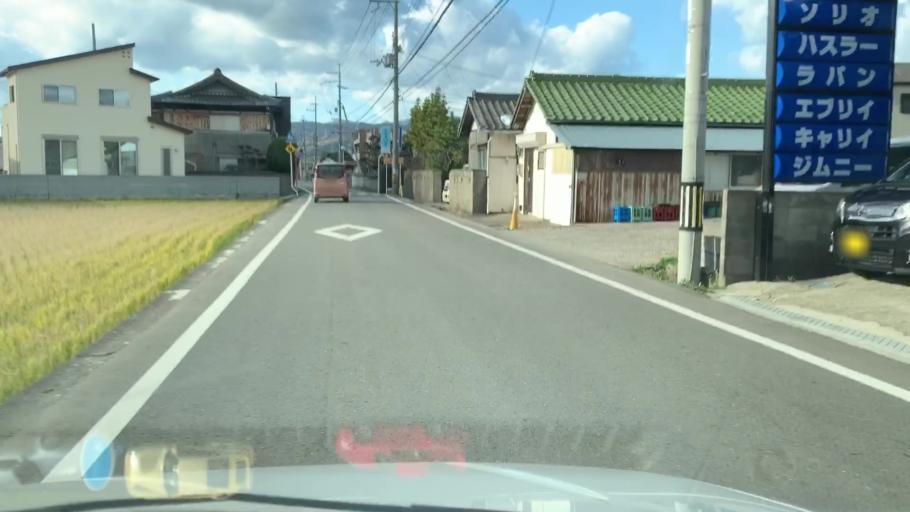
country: JP
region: Wakayama
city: Iwade
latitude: 34.2664
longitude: 135.2931
